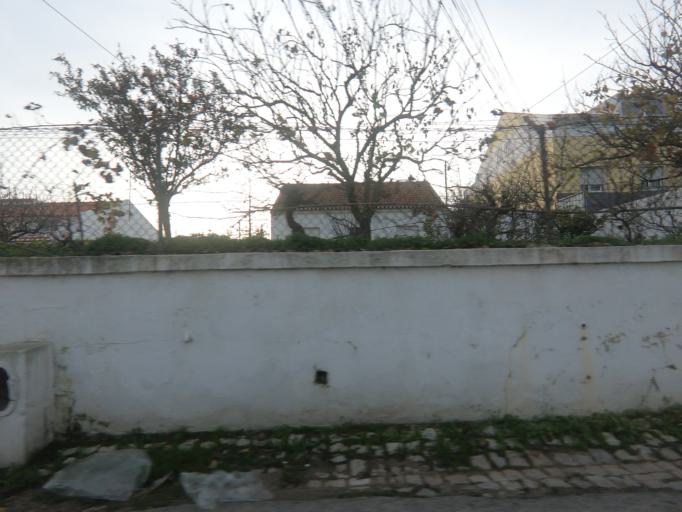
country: PT
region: Setubal
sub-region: Setubal
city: Setubal
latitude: 38.5236
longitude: -8.8520
